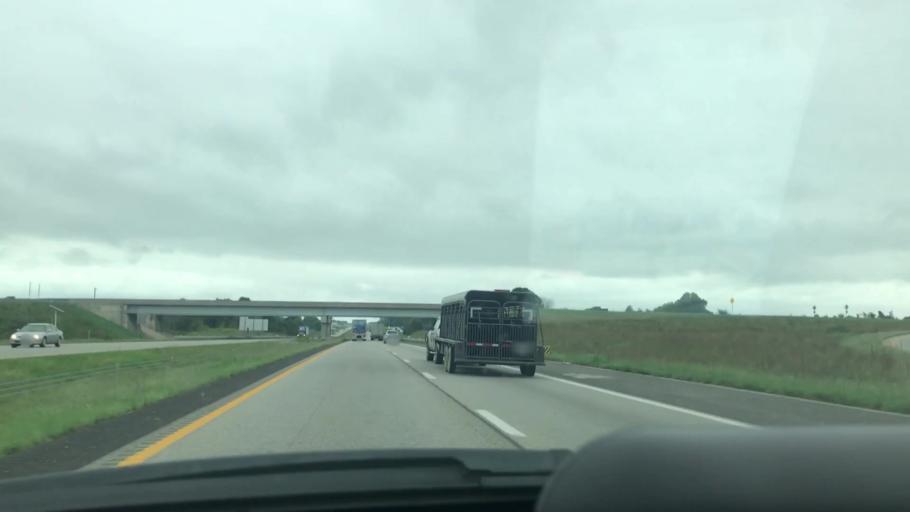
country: US
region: Missouri
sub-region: Greene County
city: Republic
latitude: 37.1955
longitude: -93.4466
